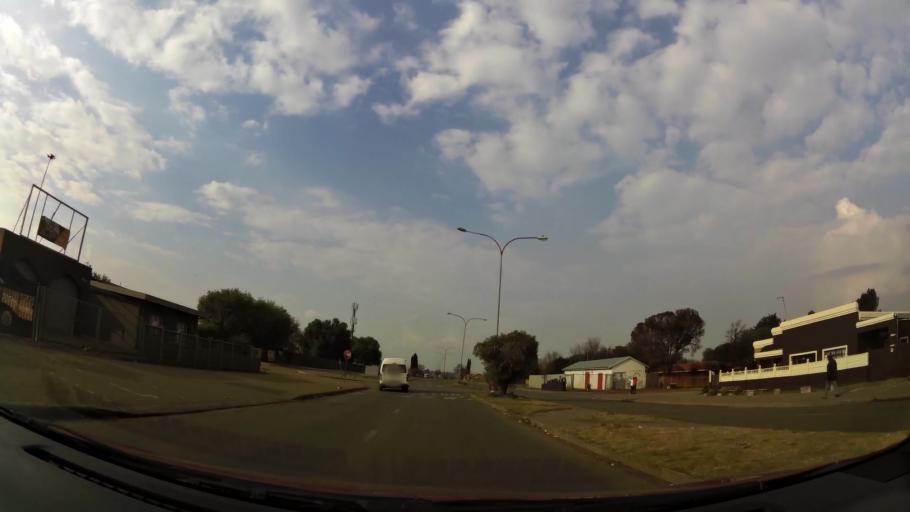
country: ZA
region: Gauteng
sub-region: Sedibeng District Municipality
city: Vanderbijlpark
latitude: -26.6834
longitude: 27.8775
